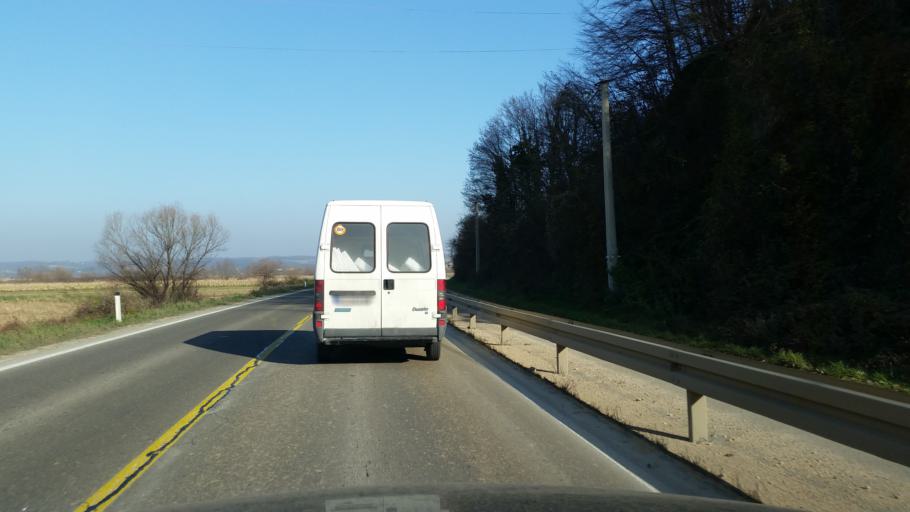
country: RS
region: Central Serbia
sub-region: Kolubarski Okrug
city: Ljig
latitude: 44.2390
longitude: 20.2653
